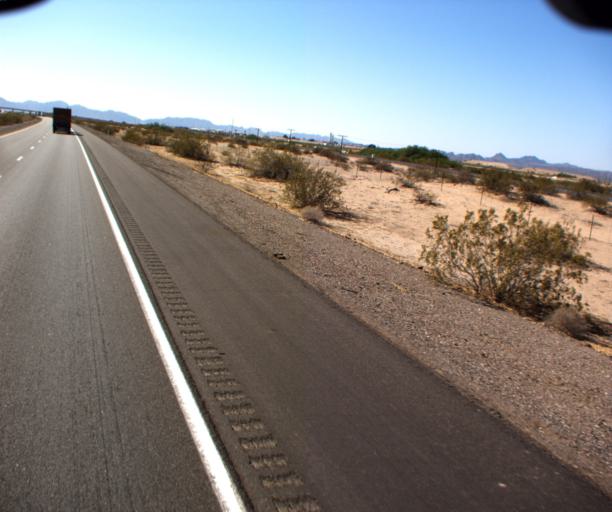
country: US
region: Arizona
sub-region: Yuma County
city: Wellton
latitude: 32.6725
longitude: -114.0963
